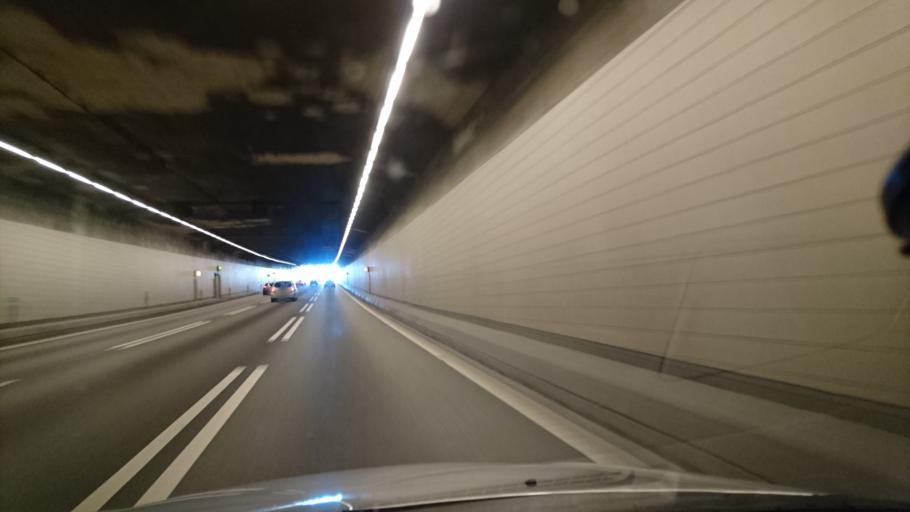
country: DK
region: North Denmark
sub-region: Alborg Kommune
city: Aalborg
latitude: 57.0545
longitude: 9.9622
